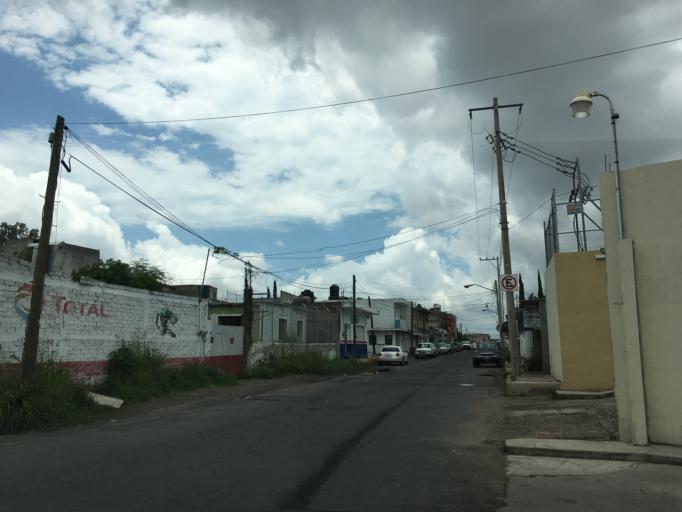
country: MX
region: Nayarit
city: Xalisco
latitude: 21.4704
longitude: -104.8875
